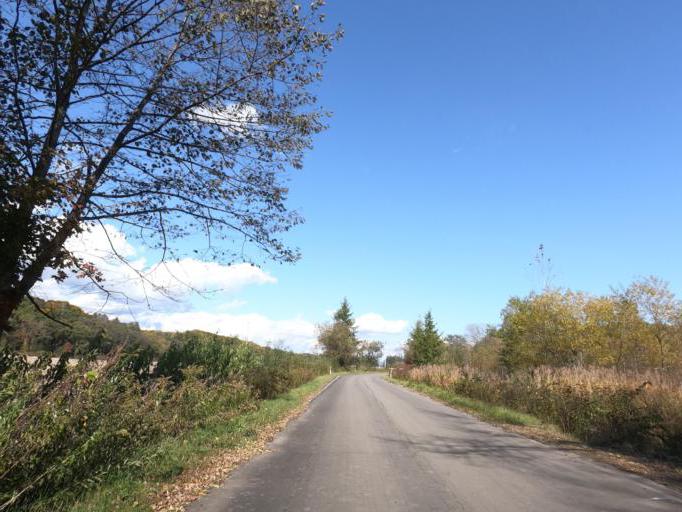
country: JP
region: Hokkaido
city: Otofuke
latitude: 43.2338
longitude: 143.2648
